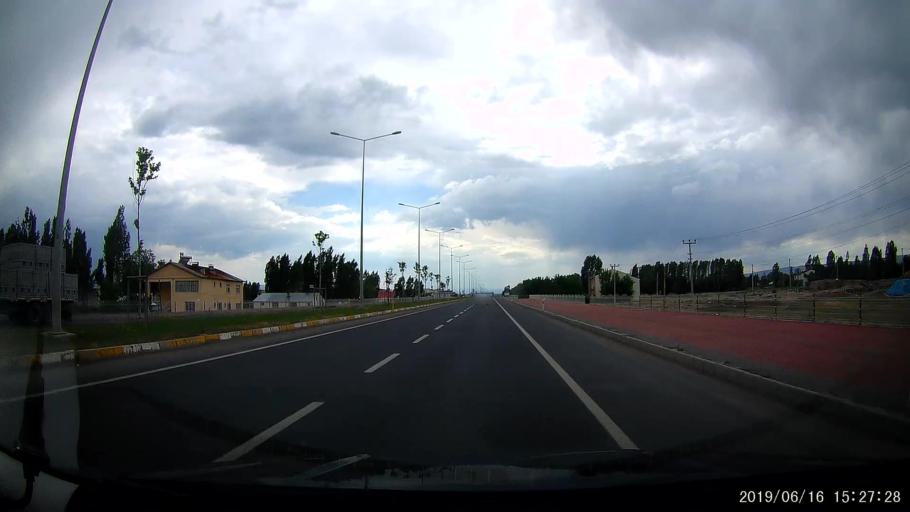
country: TR
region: Erzurum
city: Horasan
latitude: 40.0359
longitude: 42.1586
